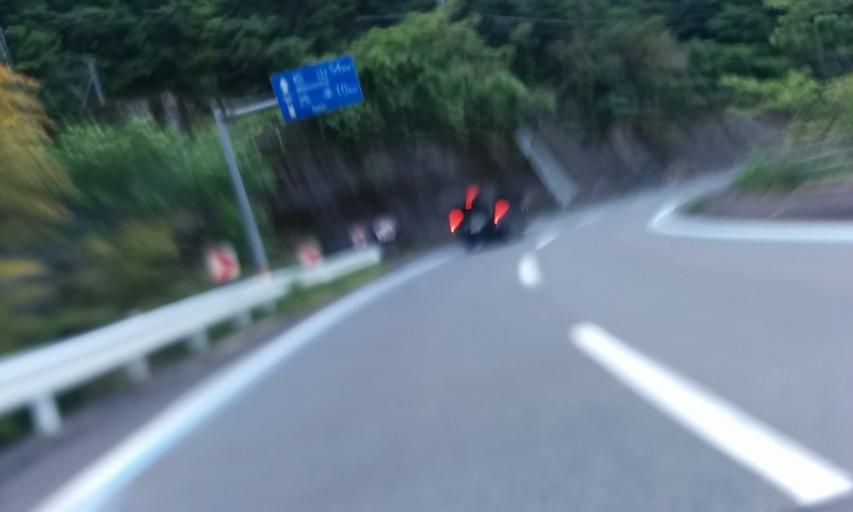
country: JP
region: Ehime
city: Saijo
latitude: 33.8497
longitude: 133.2010
